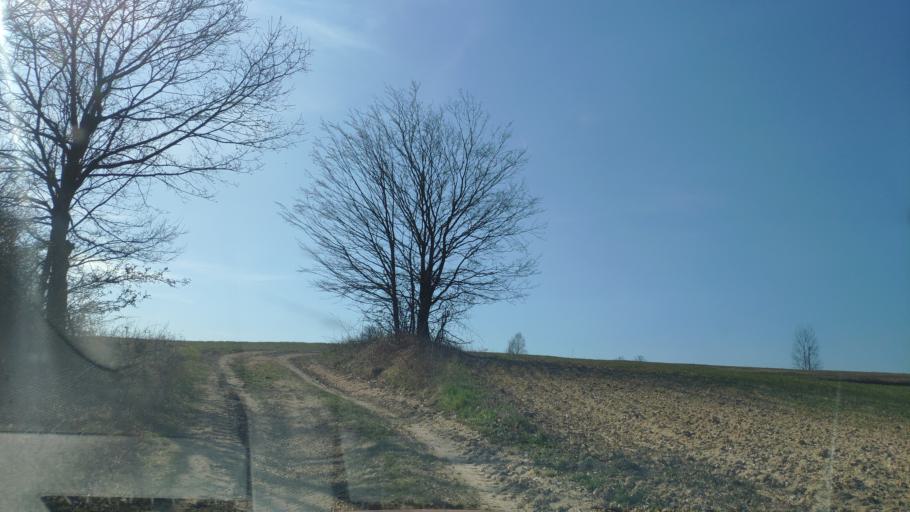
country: SK
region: Banskobystricky
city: Revuca
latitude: 48.5494
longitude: 20.2691
